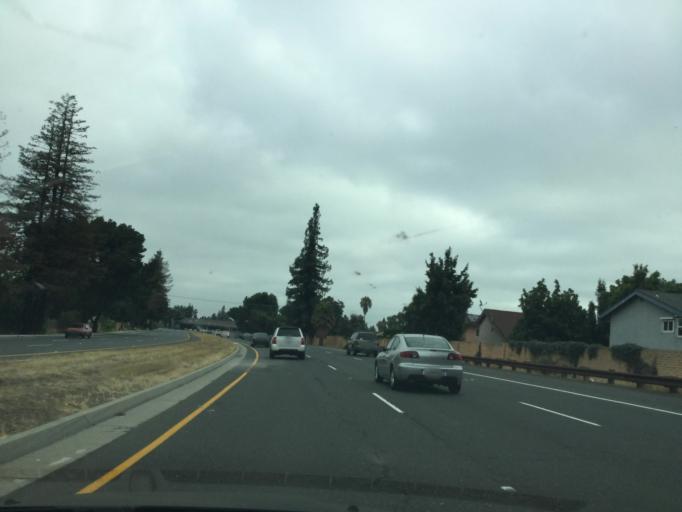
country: US
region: California
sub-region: Santa Clara County
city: Campbell
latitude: 37.3118
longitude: -121.9630
